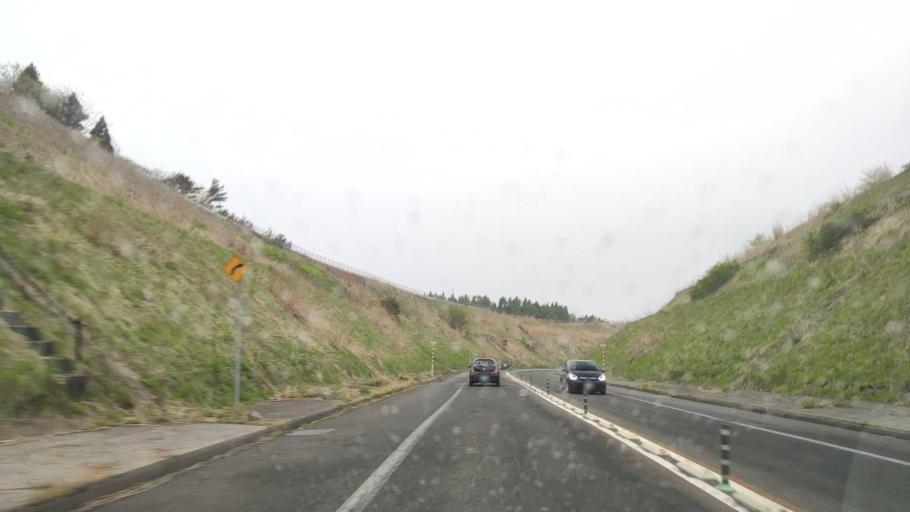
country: JP
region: Akita
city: Noshiromachi
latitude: 40.2096
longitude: 140.1932
